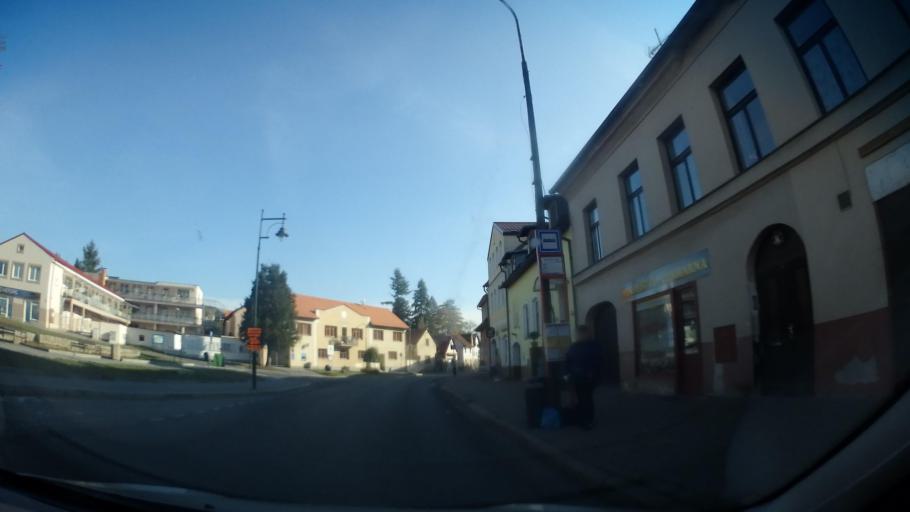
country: CZ
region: Central Bohemia
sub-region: Okres Praha-Vychod
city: Mnichovice
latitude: 49.9359
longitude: 14.7095
